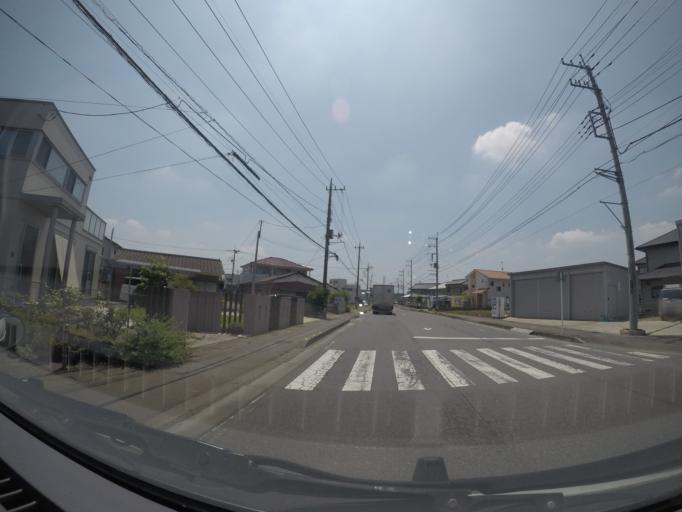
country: JP
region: Tochigi
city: Oyama
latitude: 36.2566
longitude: 139.7572
